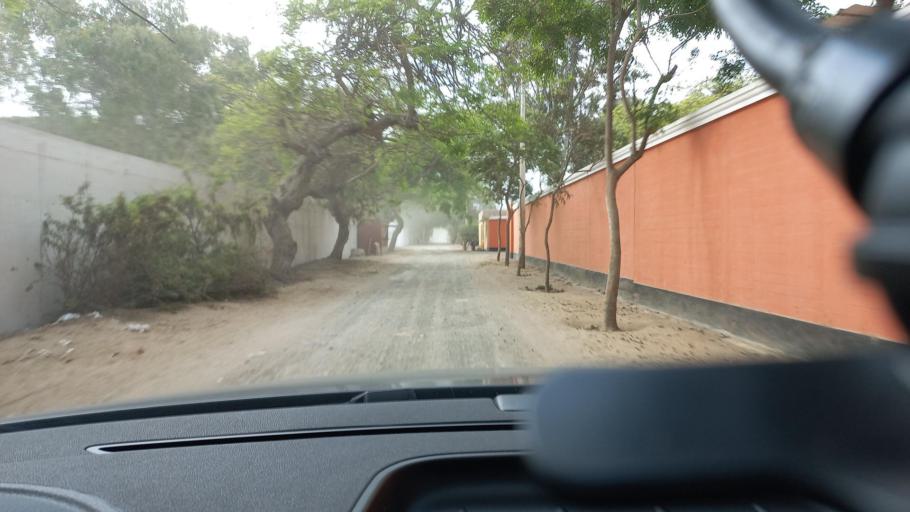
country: PE
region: Lima
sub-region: Lima
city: Punta Hermosa
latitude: -12.2606
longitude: -76.9092
